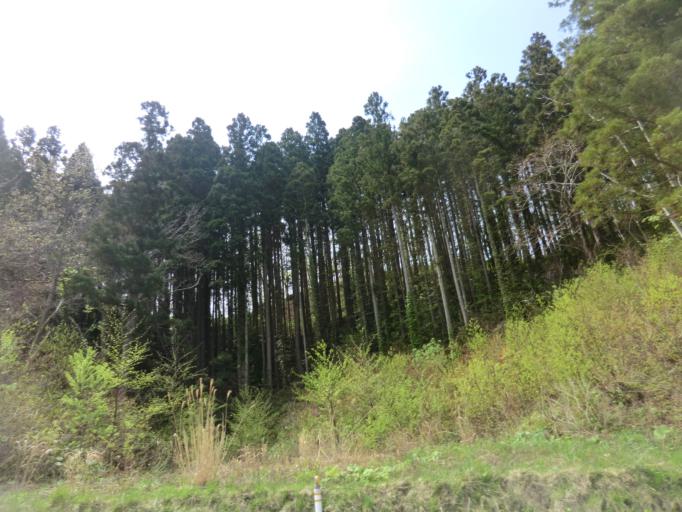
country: JP
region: Aomori
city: Mutsu
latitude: 41.3648
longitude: 140.8273
